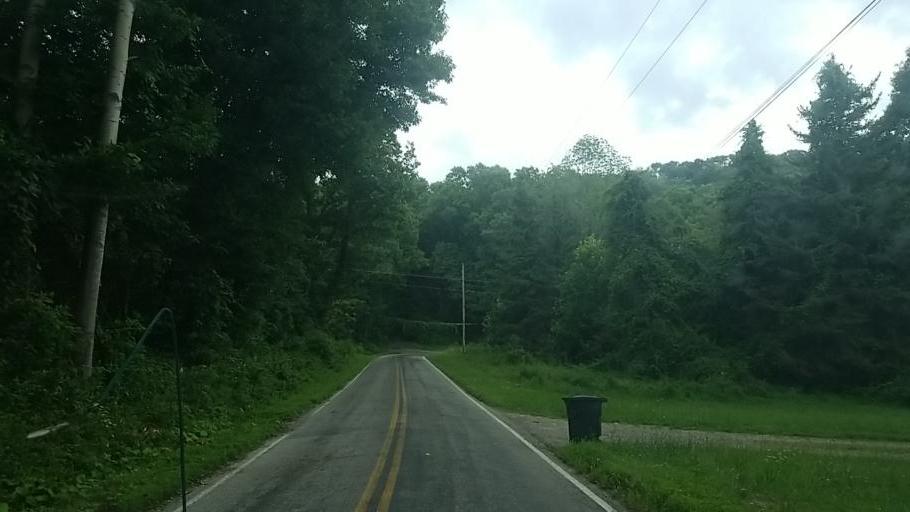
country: US
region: Ohio
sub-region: Muskingum County
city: Frazeysburg
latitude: 40.1624
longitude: -82.2582
